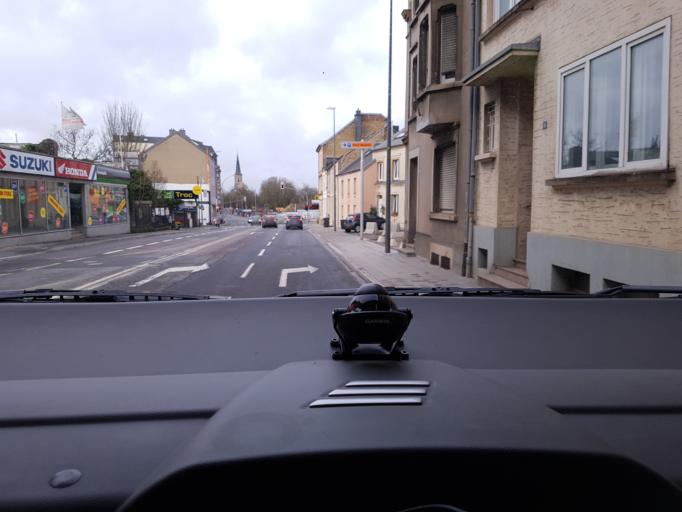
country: LU
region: Luxembourg
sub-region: Canton de Luxembourg
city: Luxembourg
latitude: 49.5989
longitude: 6.1239
